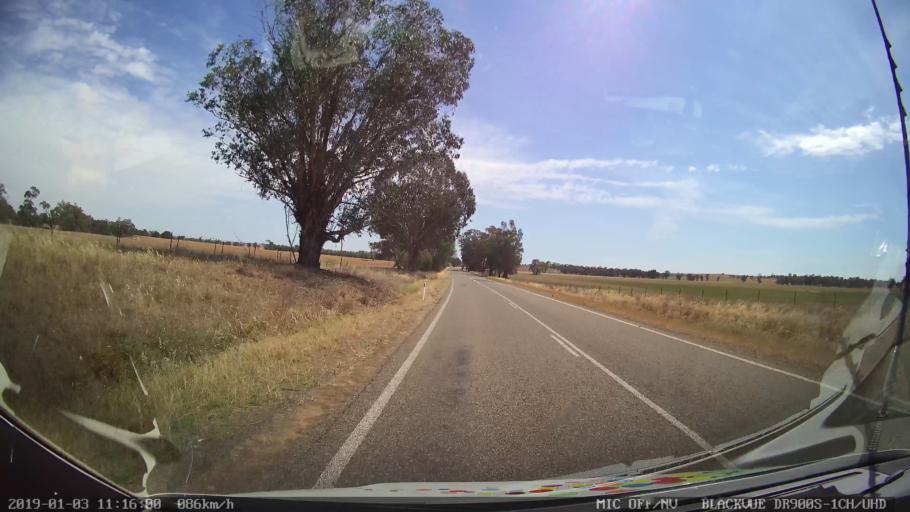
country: AU
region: New South Wales
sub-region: Young
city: Young
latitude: -34.1575
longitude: 148.2687
